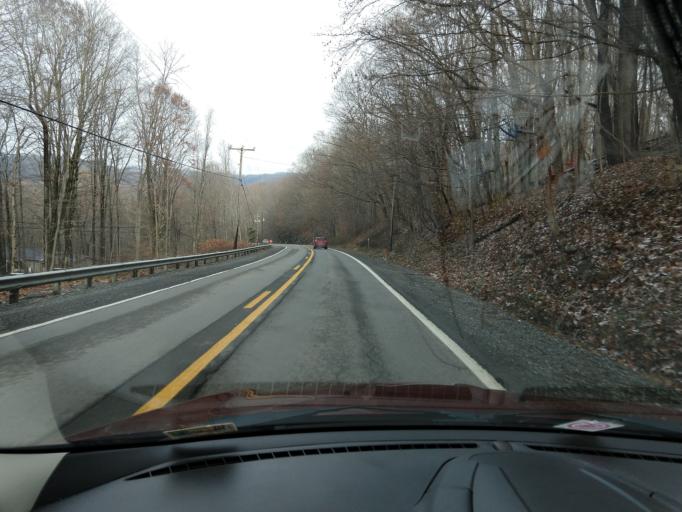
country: US
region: West Virginia
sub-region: Greenbrier County
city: Rainelle
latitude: 38.0305
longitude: -80.7272
